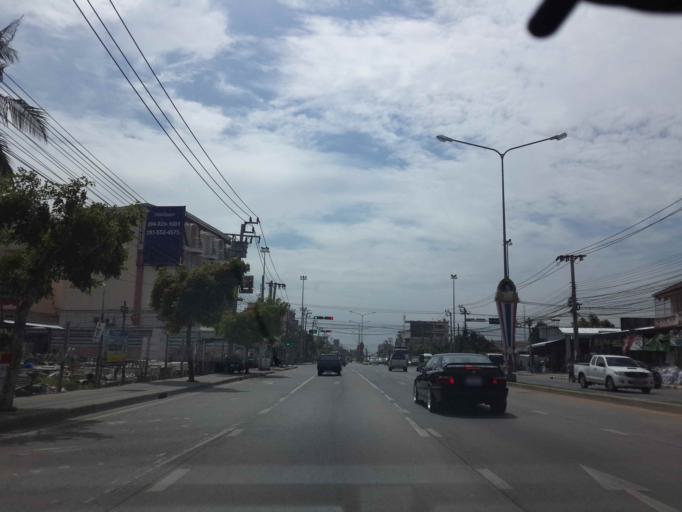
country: TH
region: Bangkok
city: Khan Na Yao
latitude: 13.8588
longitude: 100.6922
